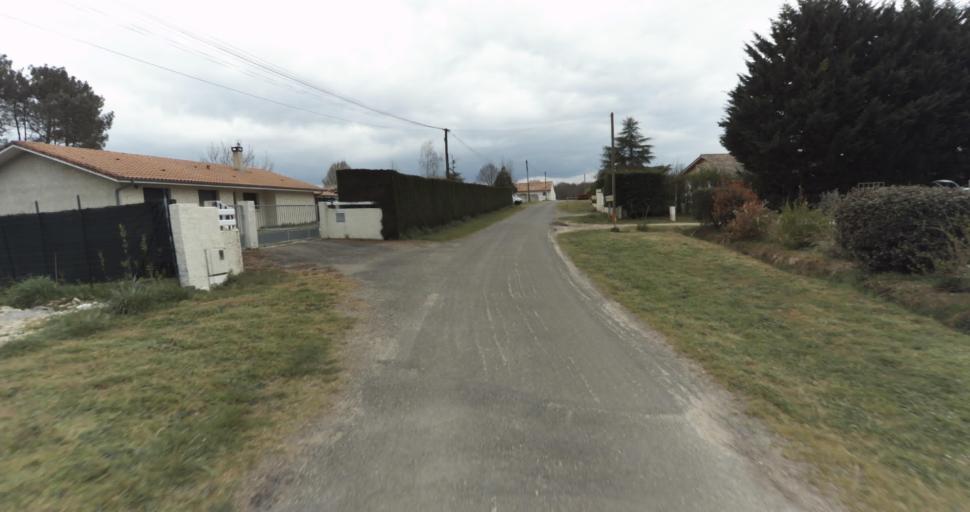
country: FR
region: Aquitaine
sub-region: Departement des Landes
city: Roquefort
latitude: 44.0226
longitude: -0.3361
